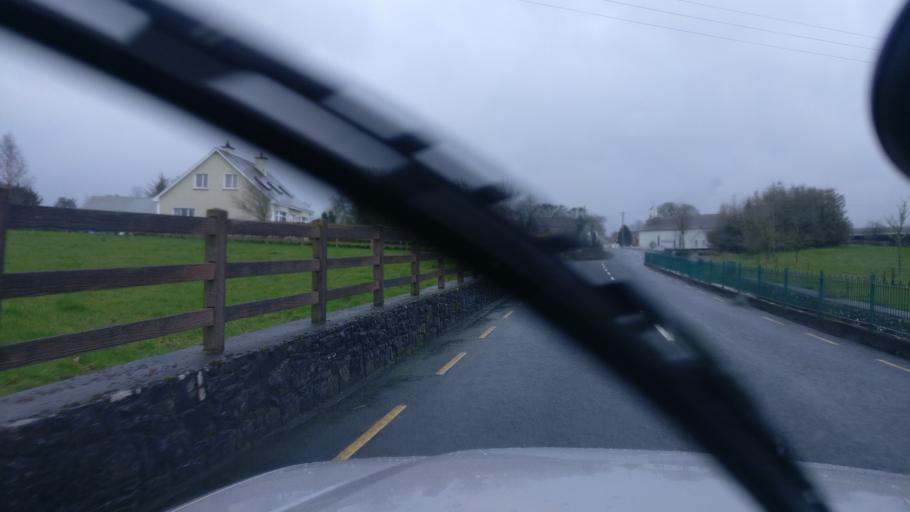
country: IE
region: Connaught
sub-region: County Galway
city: Portumna
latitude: 53.1041
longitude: -8.3893
